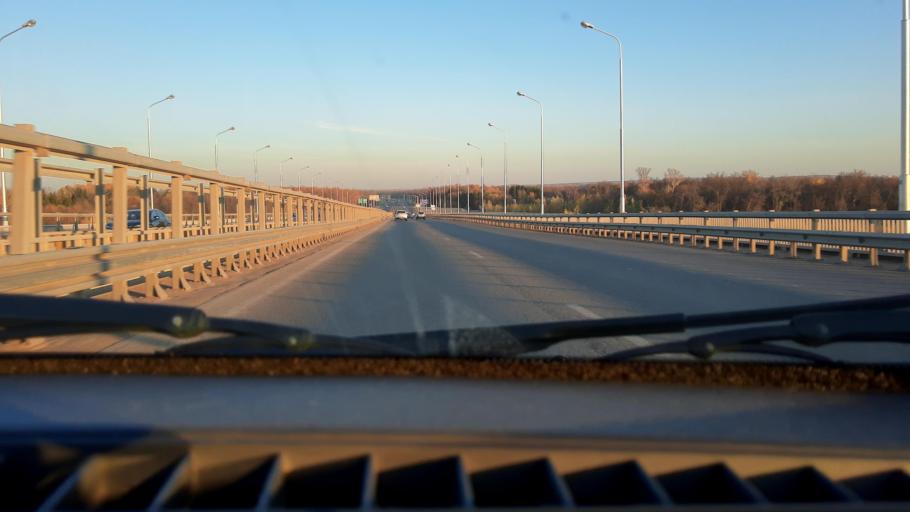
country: RU
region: Bashkortostan
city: Ufa
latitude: 54.6831
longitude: 55.9998
